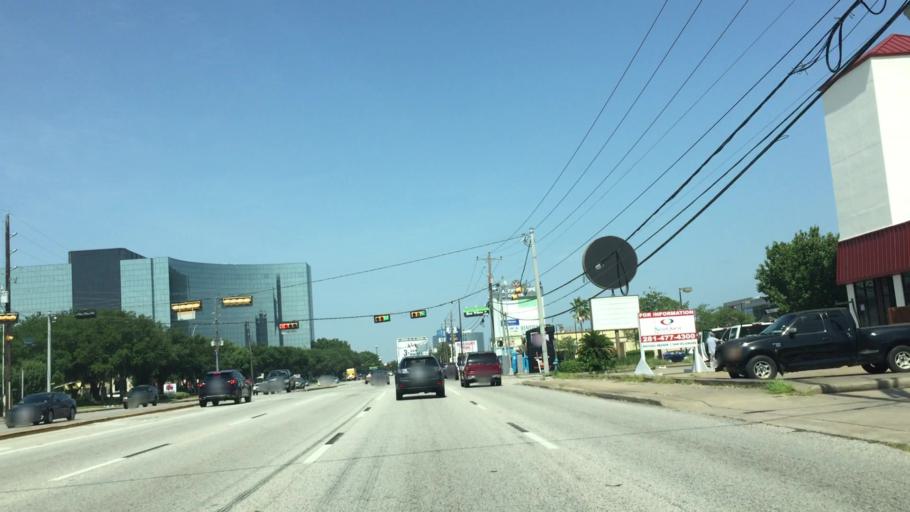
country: US
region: Texas
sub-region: Harris County
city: Bunker Hill Village
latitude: 29.7370
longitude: -95.5626
